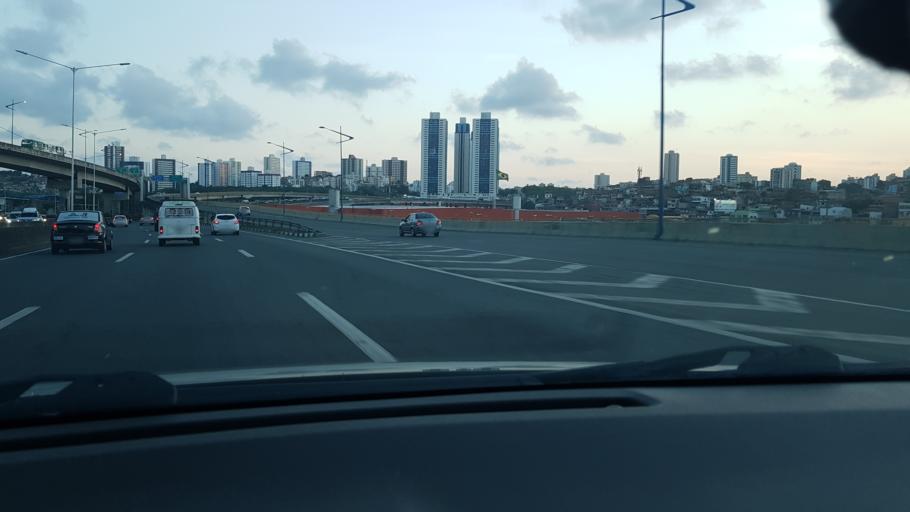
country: BR
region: Bahia
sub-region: Salvador
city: Salvador
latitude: -12.9642
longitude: -38.4771
